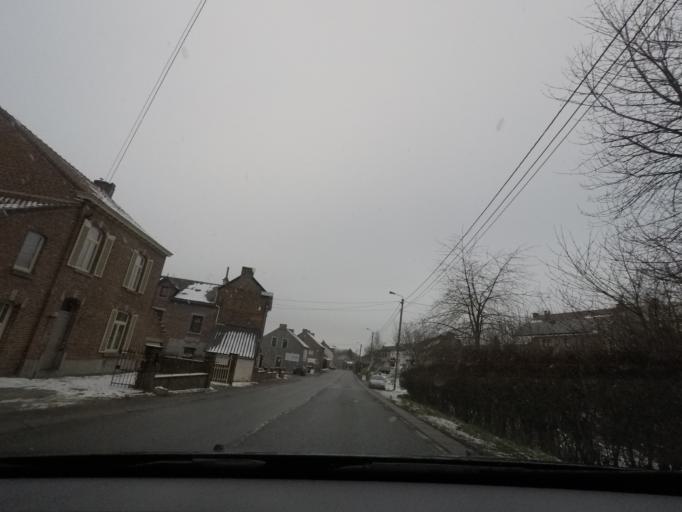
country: BE
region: Wallonia
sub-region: Province de Namur
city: Gembloux
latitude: 50.4889
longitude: 4.7005
